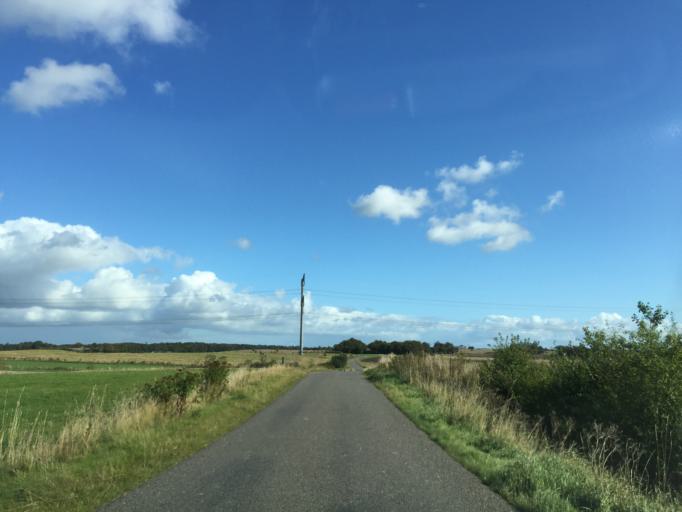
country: DK
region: Central Jutland
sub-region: Viborg Kommune
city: Bjerringbro
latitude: 56.4155
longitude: 9.5748
